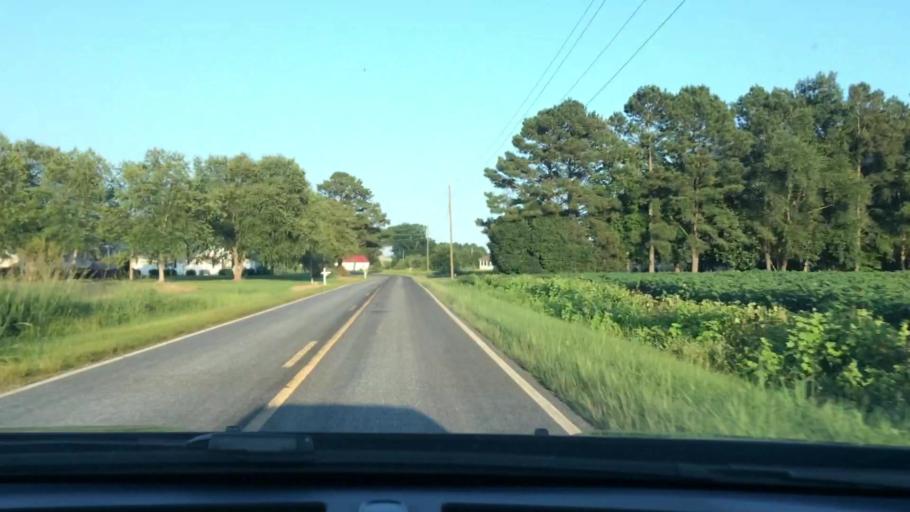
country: US
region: North Carolina
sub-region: Pitt County
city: Ayden
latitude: 35.4303
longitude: -77.4402
